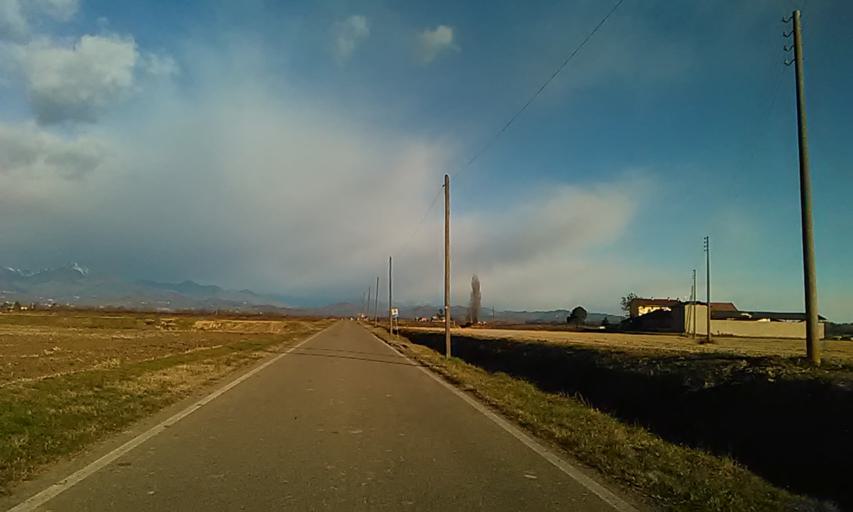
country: IT
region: Piedmont
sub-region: Provincia di Vercelli
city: Buronzo
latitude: 45.5095
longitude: 8.2701
